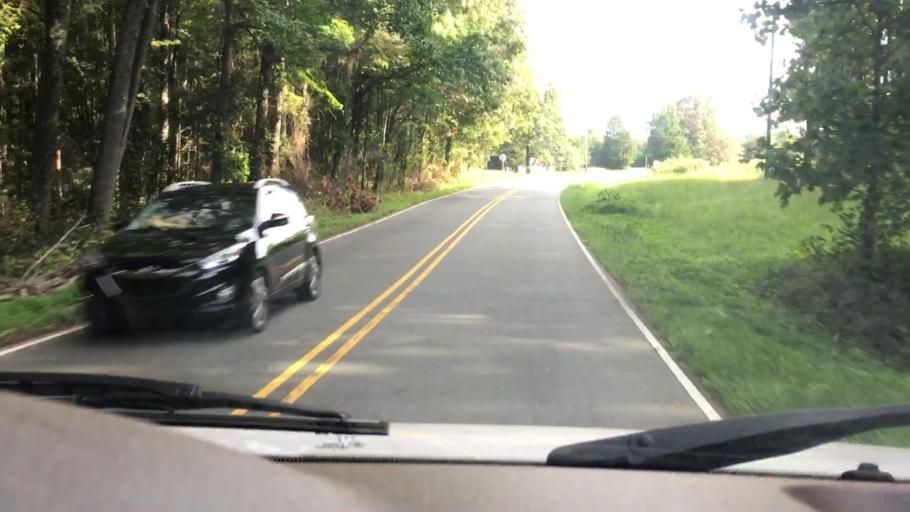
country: US
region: North Carolina
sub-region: Mecklenburg County
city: Huntersville
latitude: 35.3630
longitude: -80.8201
